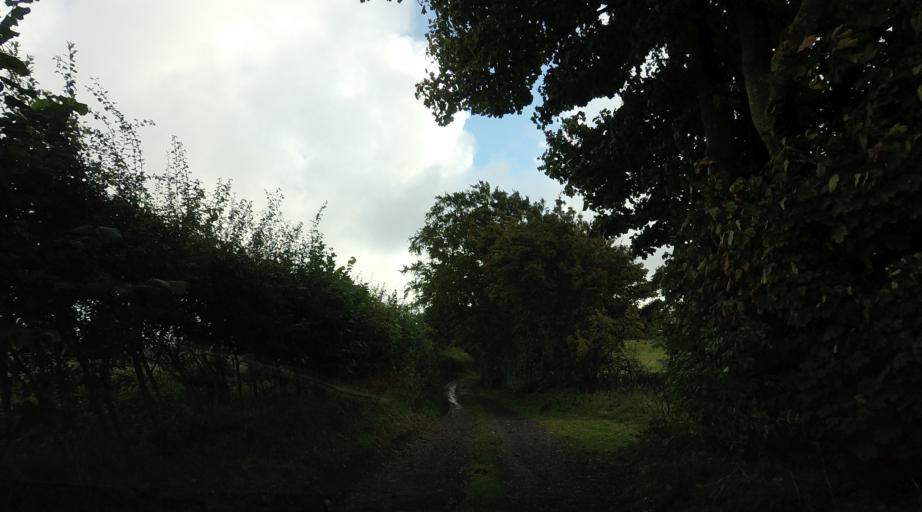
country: GB
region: Scotland
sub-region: Fife
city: Balmullo
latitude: 56.3768
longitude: -2.9581
